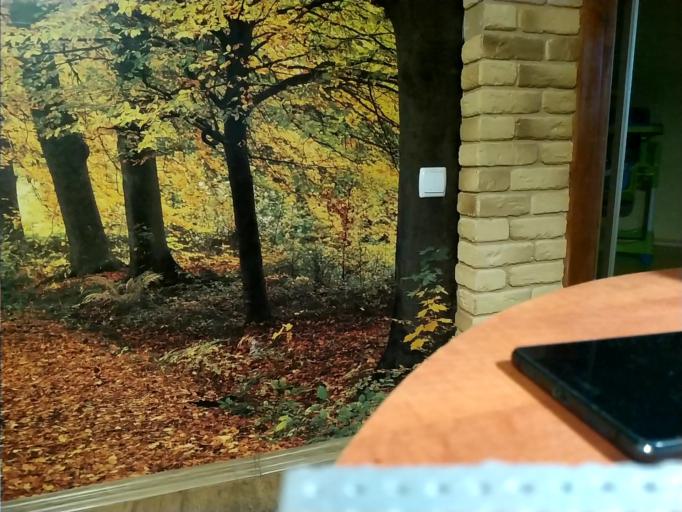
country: RU
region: Moskovskaya
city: Shevlyakovo
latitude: 56.3937
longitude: 36.8628
